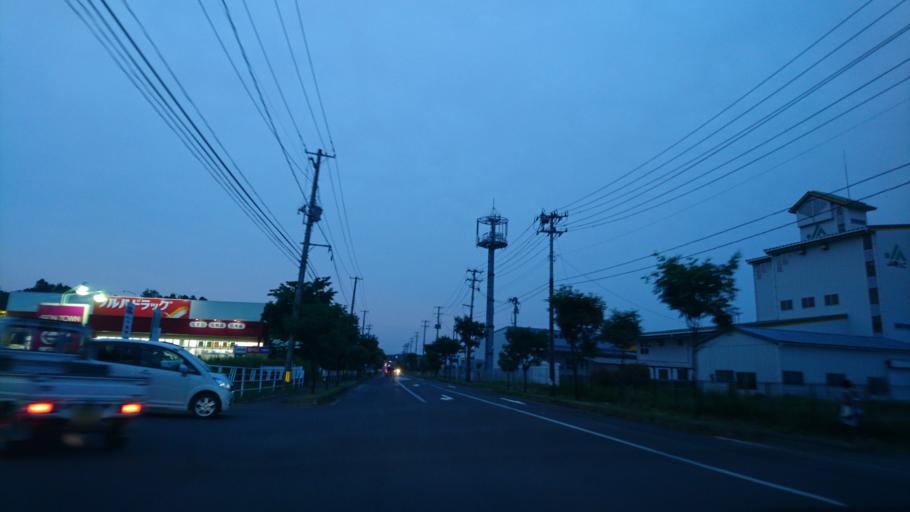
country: JP
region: Iwate
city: Ichinoseki
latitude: 38.8026
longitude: 141.0692
